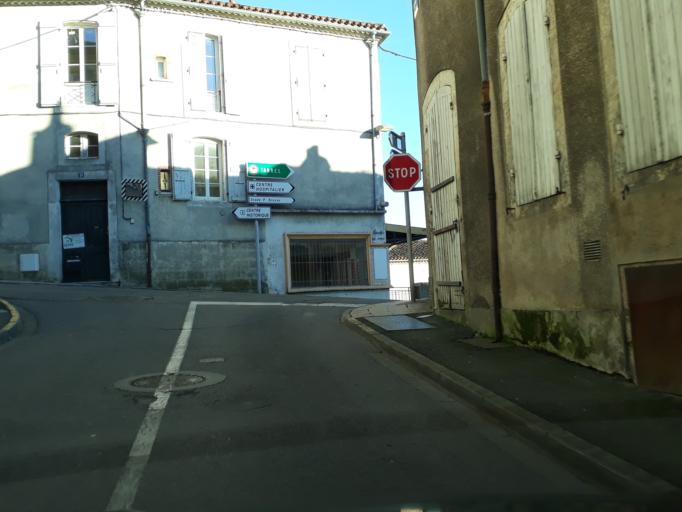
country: FR
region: Midi-Pyrenees
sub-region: Departement du Gers
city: Auch
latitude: 43.6455
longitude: 0.5822
